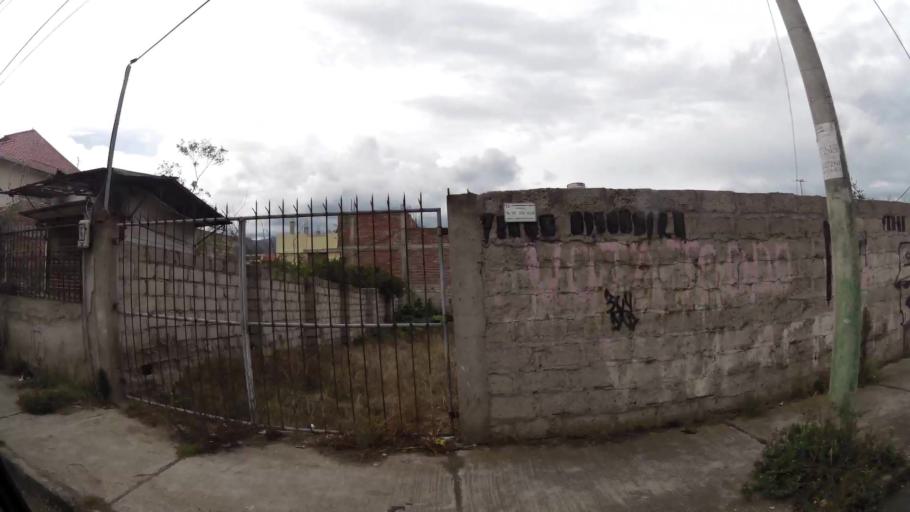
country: EC
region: Tungurahua
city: Ambato
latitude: -1.2582
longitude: -78.6271
